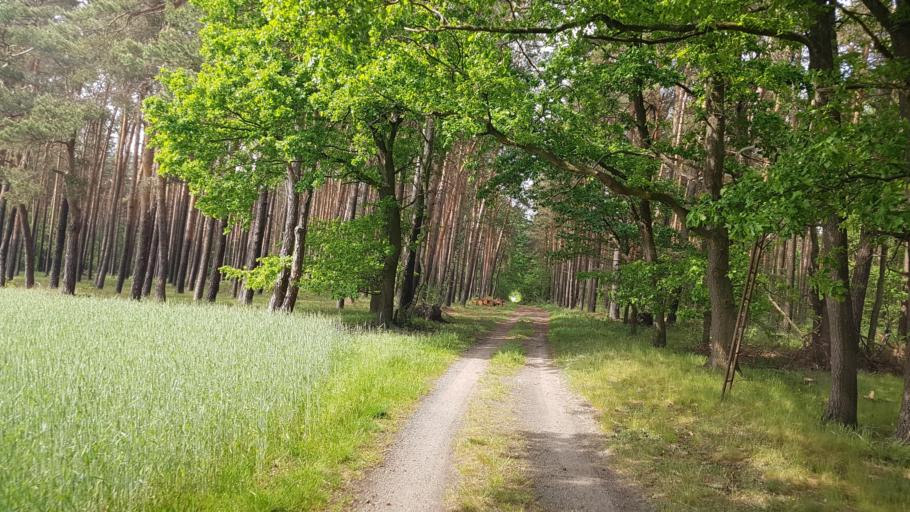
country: DE
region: Brandenburg
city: Sallgast
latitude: 51.5921
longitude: 13.8695
